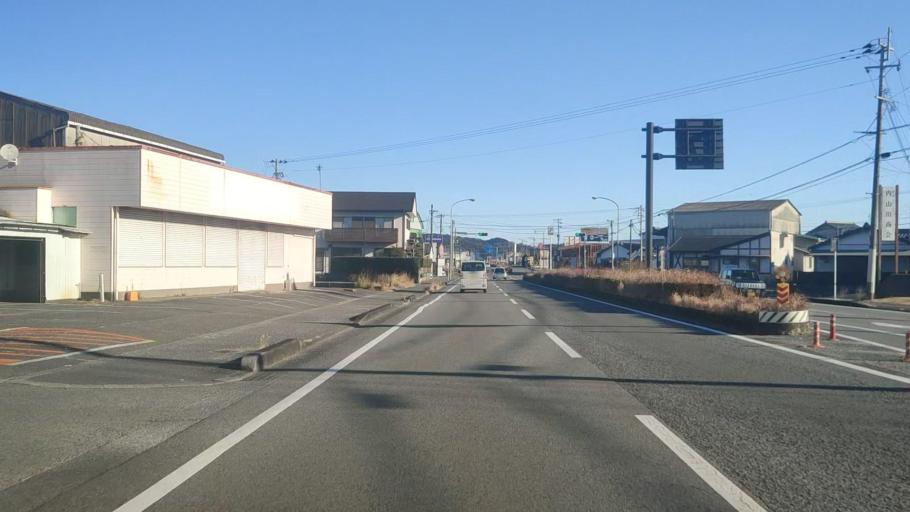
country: JP
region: Miyazaki
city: Nobeoka
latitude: 32.4749
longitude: 131.6531
